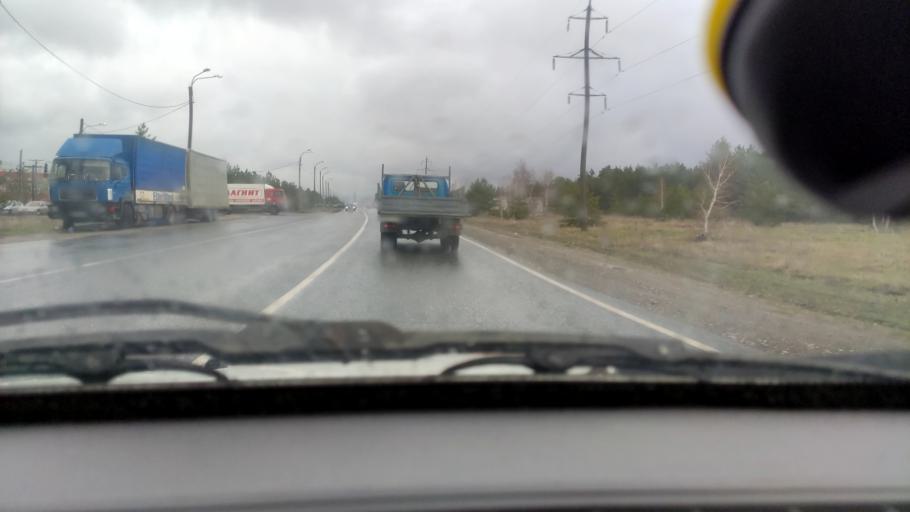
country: RU
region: Samara
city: Zhigulevsk
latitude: 53.5641
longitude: 49.5452
